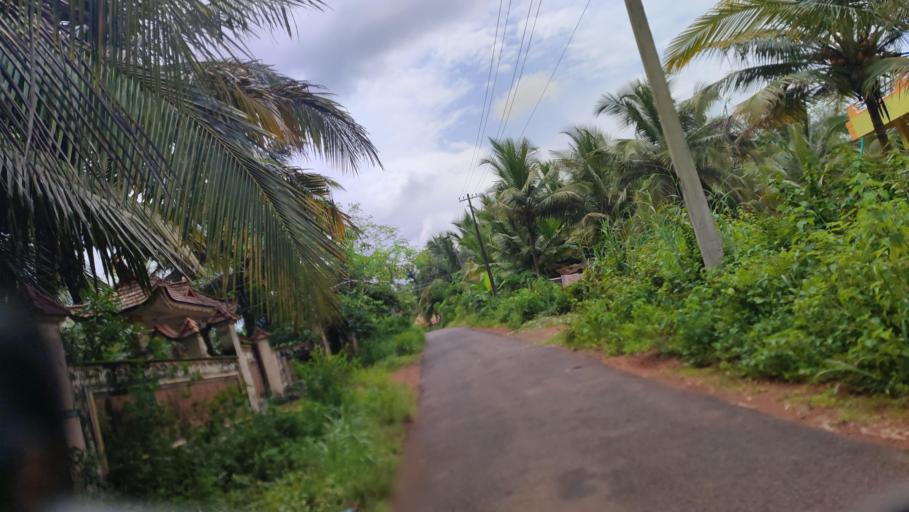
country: IN
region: Kerala
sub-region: Kasaragod District
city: Kannangad
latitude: 12.4011
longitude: 75.0565
